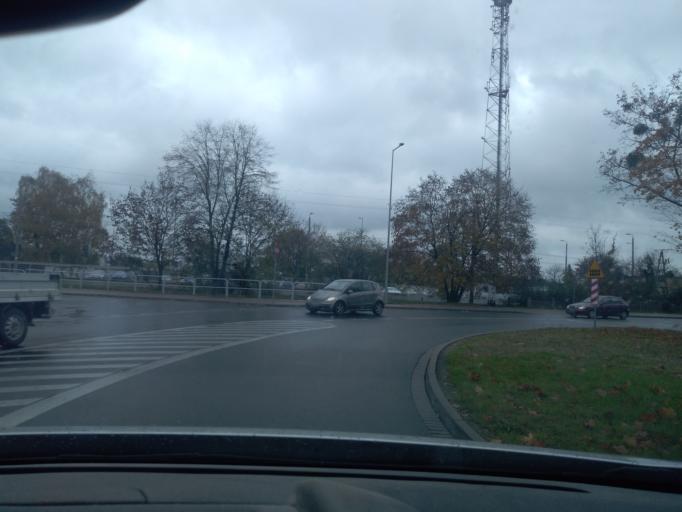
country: PL
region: Greater Poland Voivodeship
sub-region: Powiat obornicki
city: Oborniki
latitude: 52.6456
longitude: 16.8195
